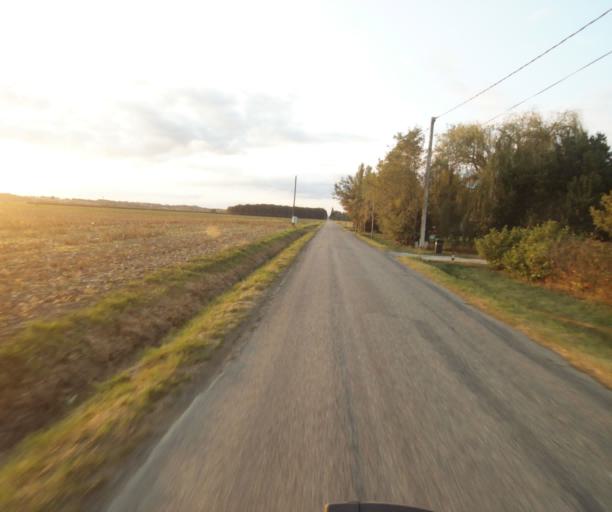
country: FR
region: Midi-Pyrenees
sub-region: Departement du Tarn-et-Garonne
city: Verdun-sur-Garonne
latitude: 43.8253
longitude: 1.2362
